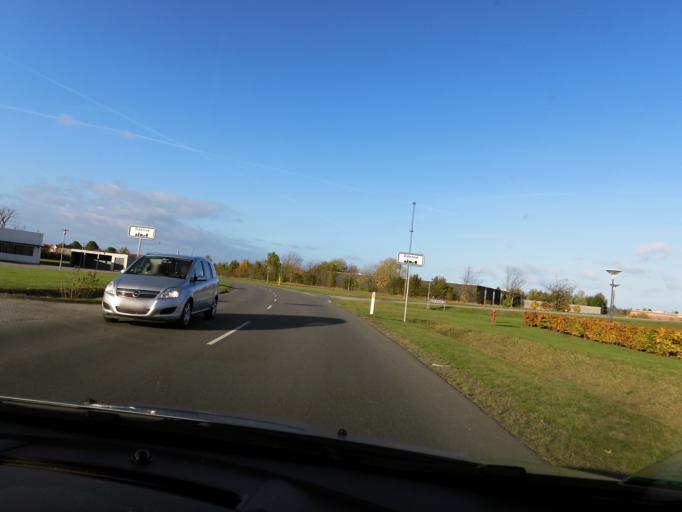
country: DK
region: South Denmark
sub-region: Odense Kommune
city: Neder Holluf
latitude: 55.3553
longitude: 10.4568
